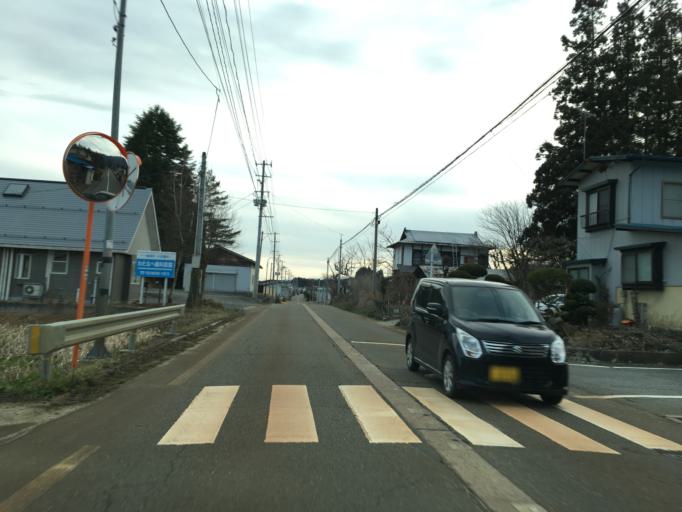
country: JP
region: Yamagata
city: Nagai
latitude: 38.1820
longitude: 140.0689
